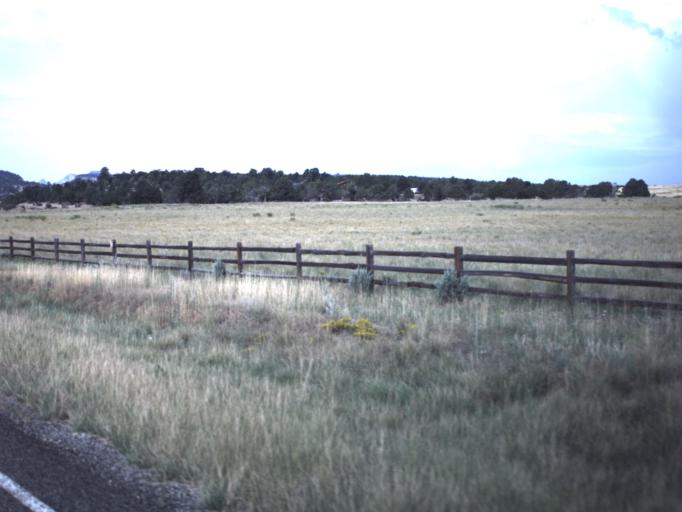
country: US
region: Utah
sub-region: Washington County
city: Hildale
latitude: 37.2438
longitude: -112.8099
